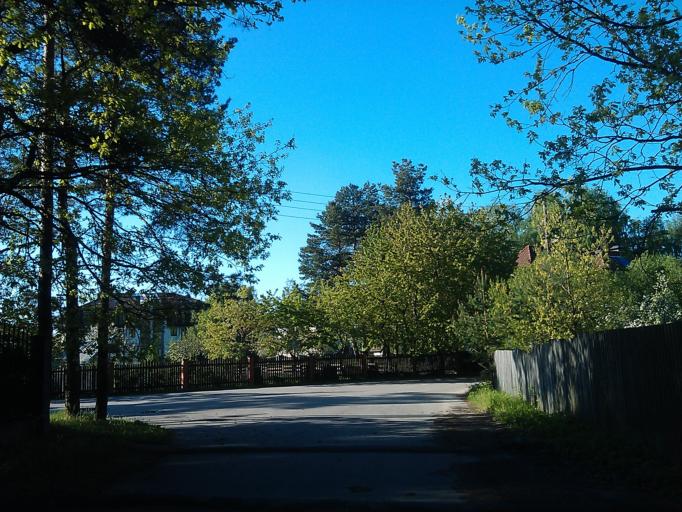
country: LV
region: Riga
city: Bergi
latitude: 57.0161
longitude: 24.2725
